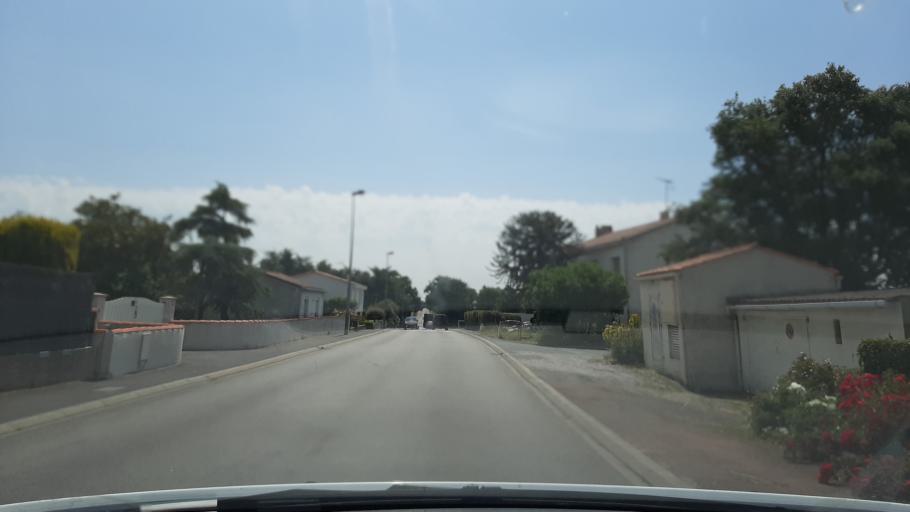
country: FR
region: Pays de la Loire
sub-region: Departement de la Vendee
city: Le Poire-sur-Vie
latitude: 46.7702
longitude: -1.5054
